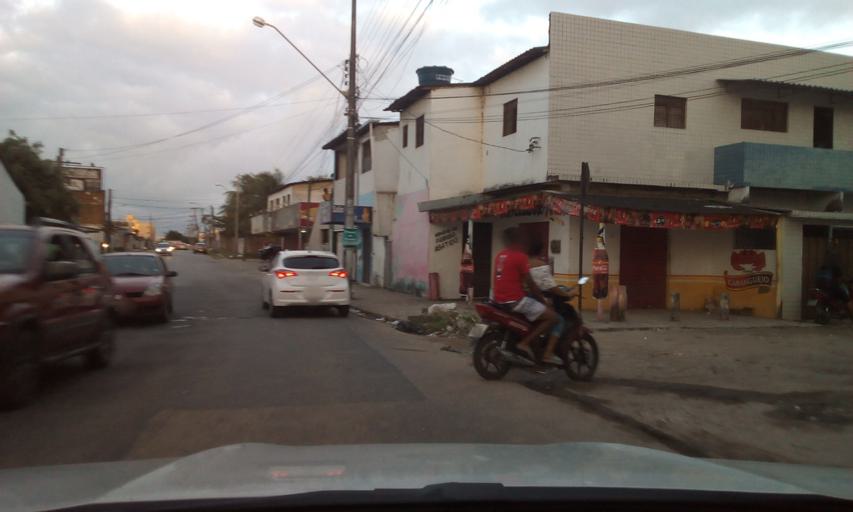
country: BR
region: Paraiba
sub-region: Joao Pessoa
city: Joao Pessoa
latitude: -7.1778
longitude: -34.8786
